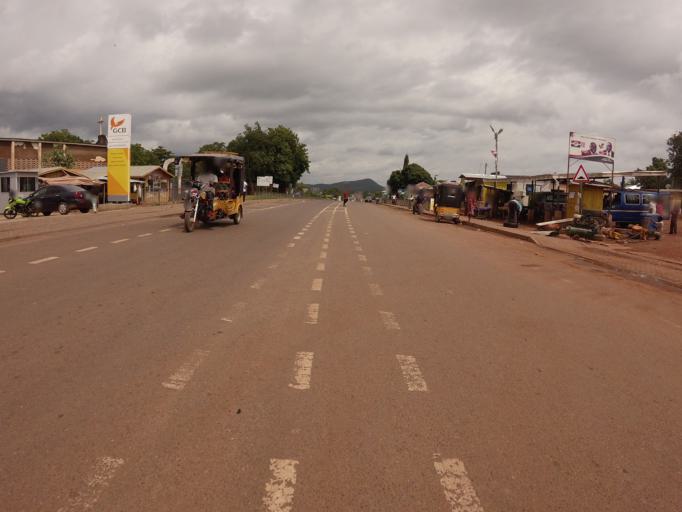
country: TG
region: Centrale
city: Sotouboua
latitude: 8.2595
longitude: 0.5220
